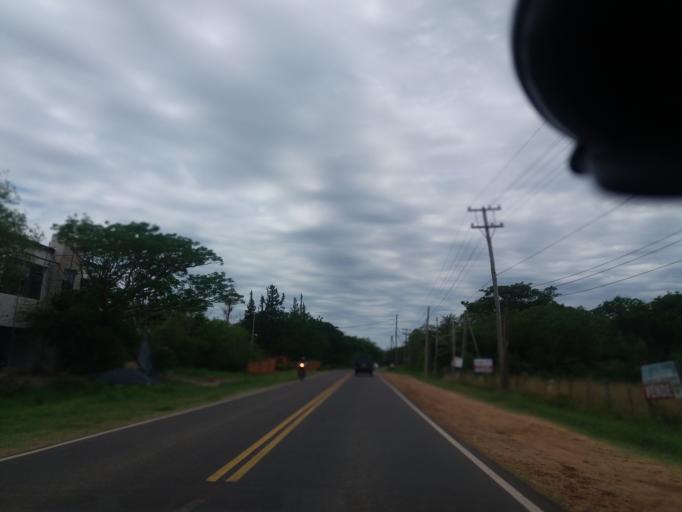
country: AR
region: Corrientes
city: Corrientes
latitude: -27.4518
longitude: -58.7294
